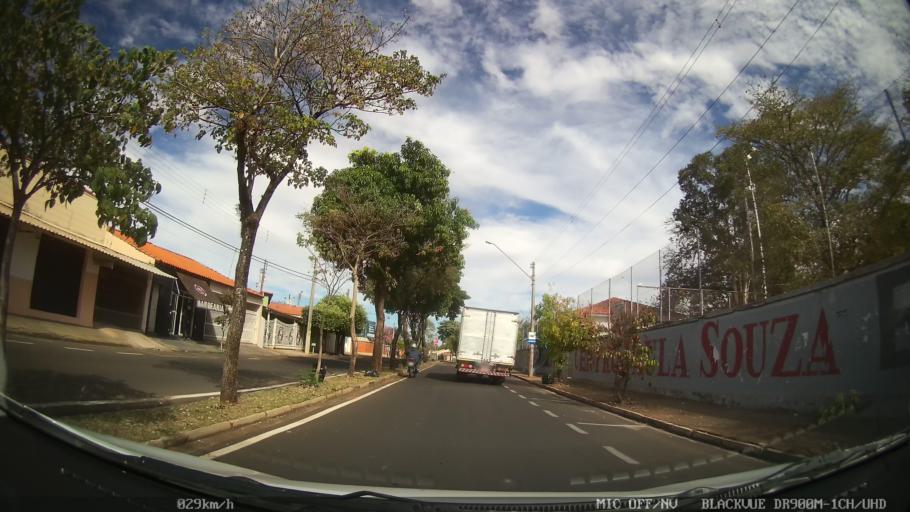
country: BR
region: Sao Paulo
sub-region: Catanduva
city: Catanduva
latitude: -21.1310
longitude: -48.9559
